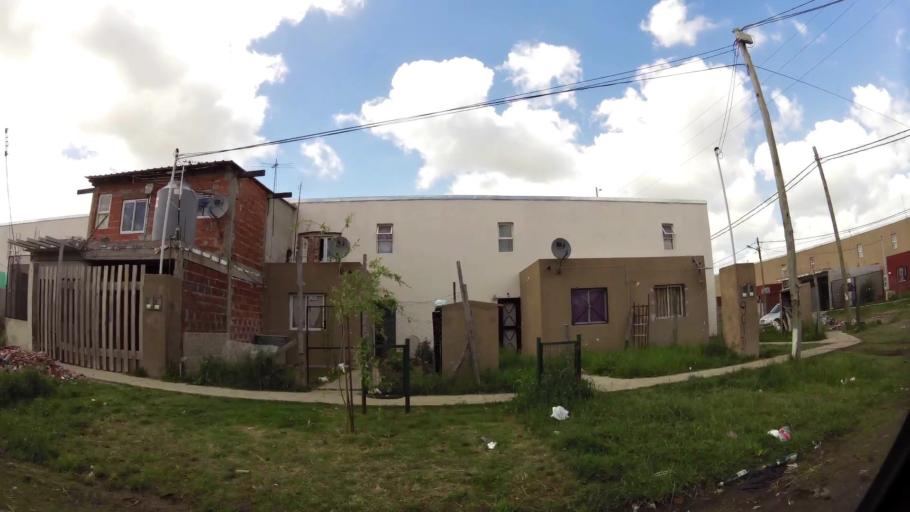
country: AR
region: Buenos Aires
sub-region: Partido de Quilmes
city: Quilmes
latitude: -34.8301
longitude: -58.2111
